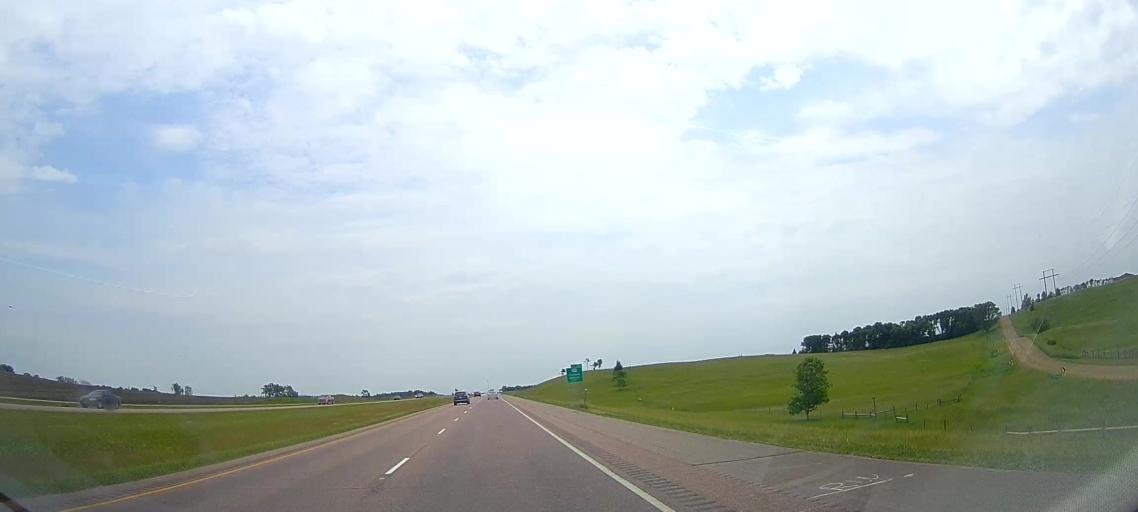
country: US
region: South Dakota
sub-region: Minnehaha County
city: Hartford
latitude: 43.6583
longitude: -97.1088
